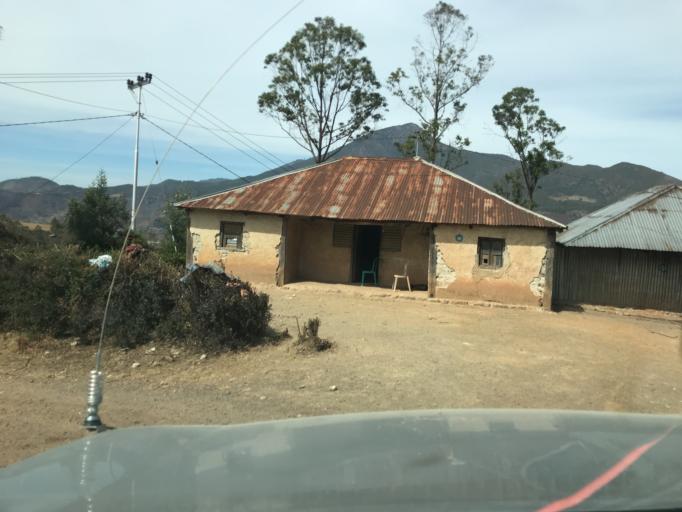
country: TL
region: Ainaro
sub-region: Ainaro
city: Ainaro
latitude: -8.8825
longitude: 125.5333
